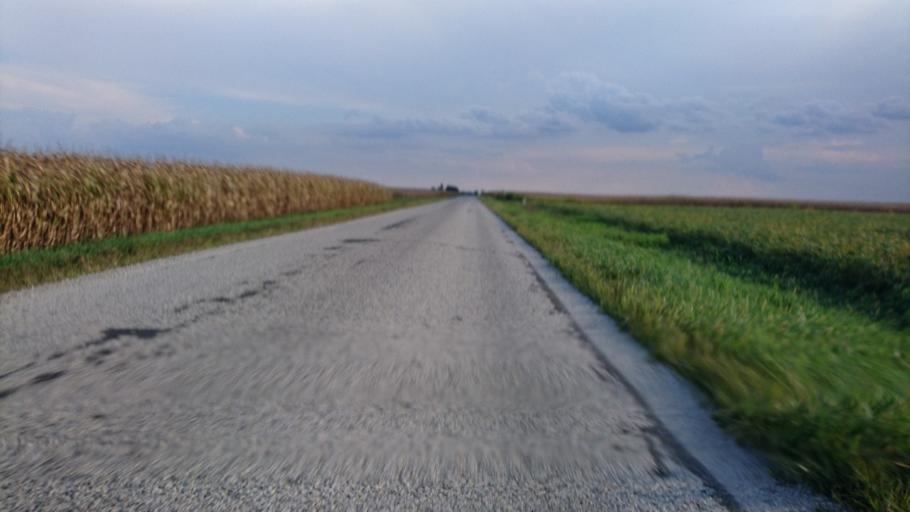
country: US
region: Illinois
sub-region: Logan County
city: Atlanta
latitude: 40.2535
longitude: -89.2052
